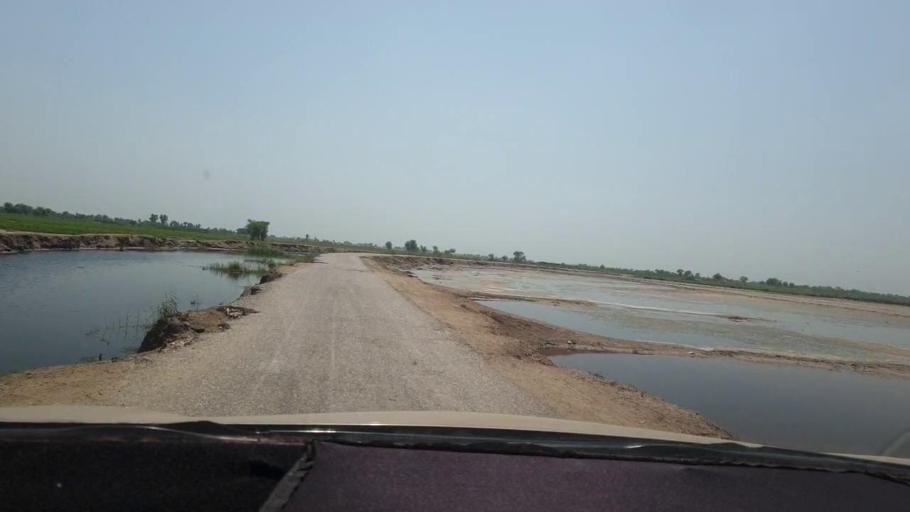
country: PK
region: Sindh
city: Shahdadkot
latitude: 27.8445
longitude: 67.9482
